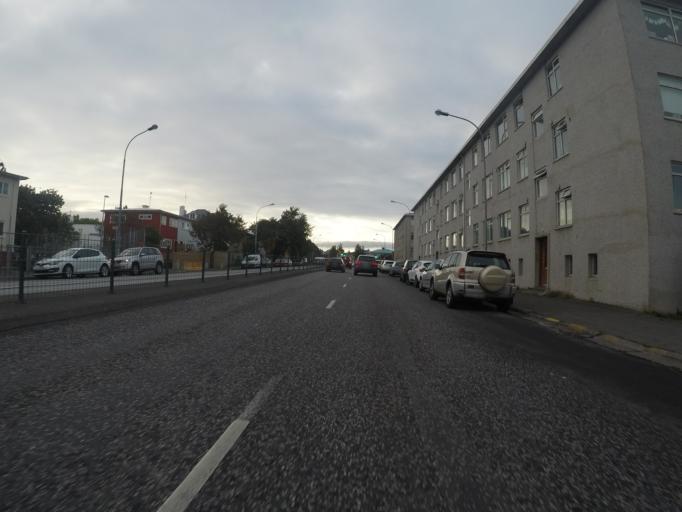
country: IS
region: Capital Region
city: Seltjarnarnes
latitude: 64.1492
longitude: -21.9592
